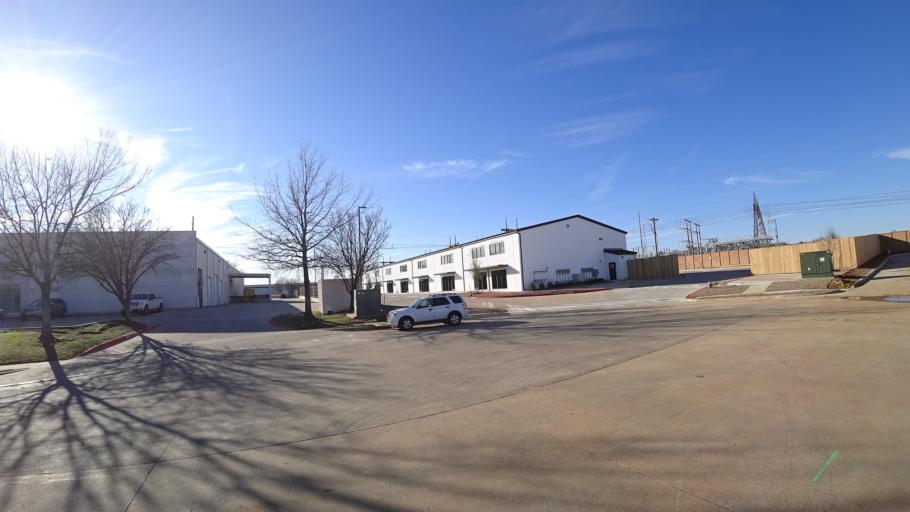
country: US
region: Texas
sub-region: Denton County
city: Lewisville
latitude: 33.0646
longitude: -97.0081
